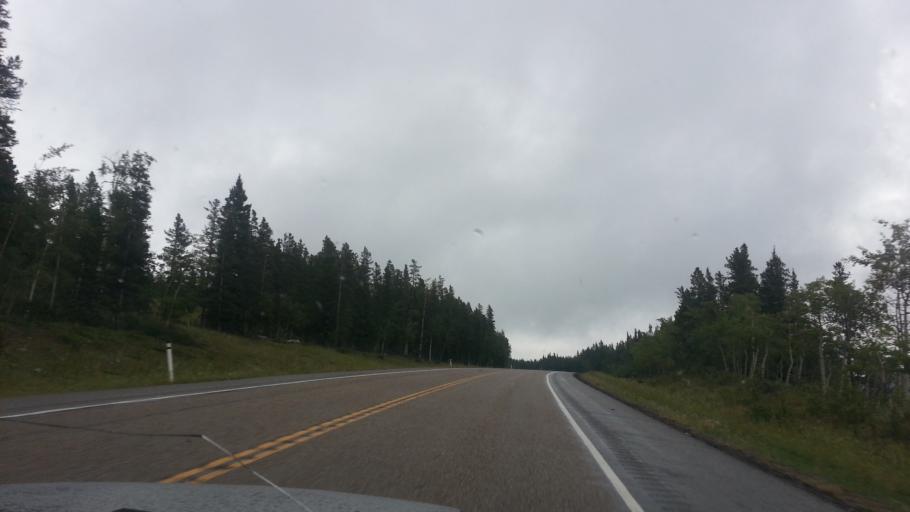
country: CA
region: Alberta
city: Cochrane
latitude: 50.8692
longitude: -114.7768
